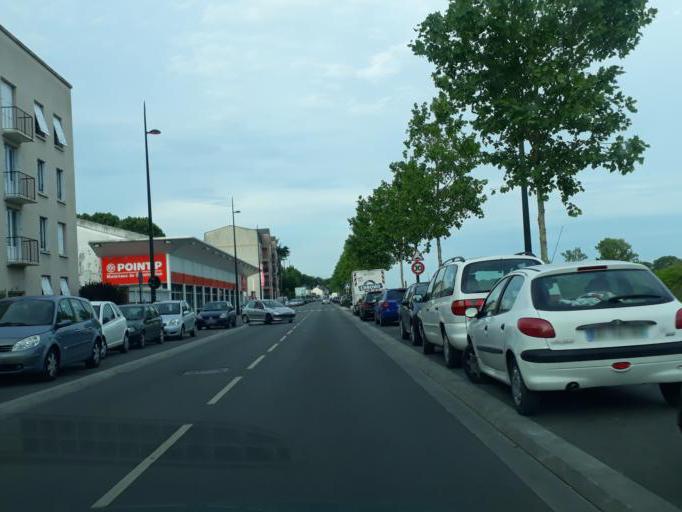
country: FR
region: Centre
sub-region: Departement du Loiret
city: Saint-Jean-le-Blanc
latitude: 47.8997
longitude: 1.9252
